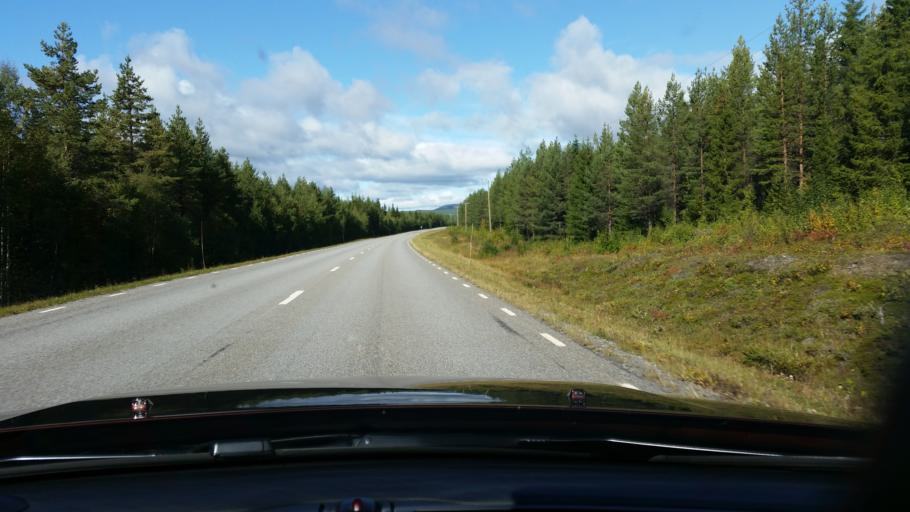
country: SE
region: Jaemtland
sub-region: Stroemsunds Kommun
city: Stroemsund
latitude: 64.2832
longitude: 15.3566
